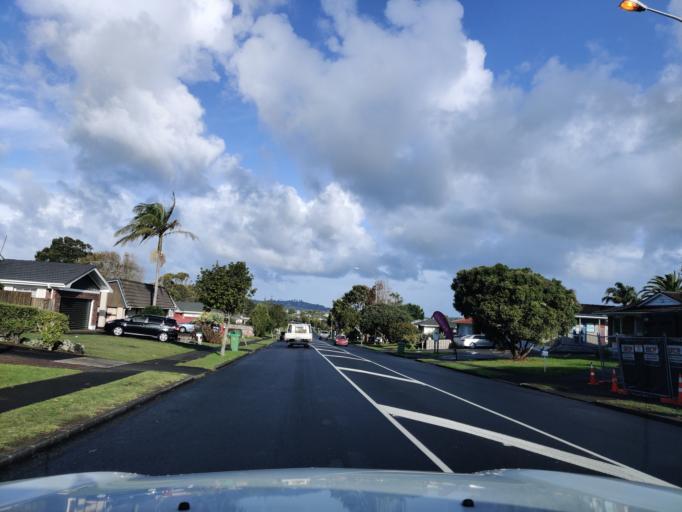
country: NZ
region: Auckland
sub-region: Auckland
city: Pakuranga
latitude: -36.9071
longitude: 174.8969
